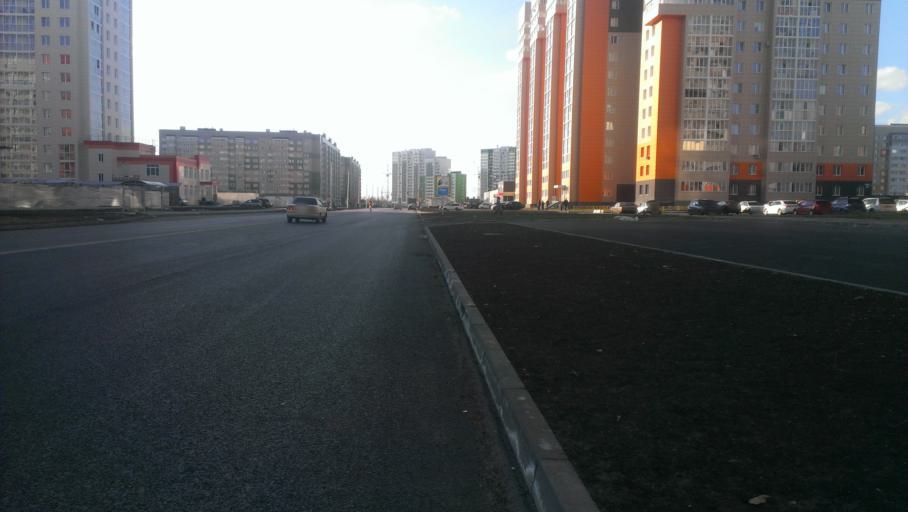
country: RU
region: Altai Krai
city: Novosilikatnyy
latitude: 53.3372
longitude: 83.6582
